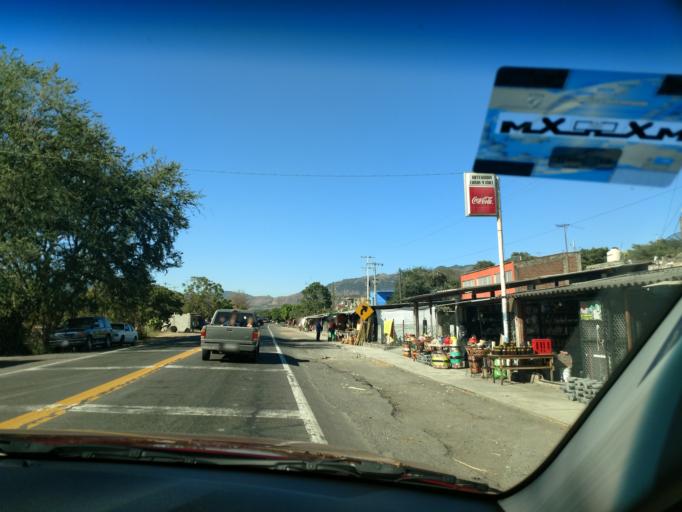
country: MX
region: Nayarit
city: San Pedro Lagunillas
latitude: 21.1565
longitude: -104.6251
